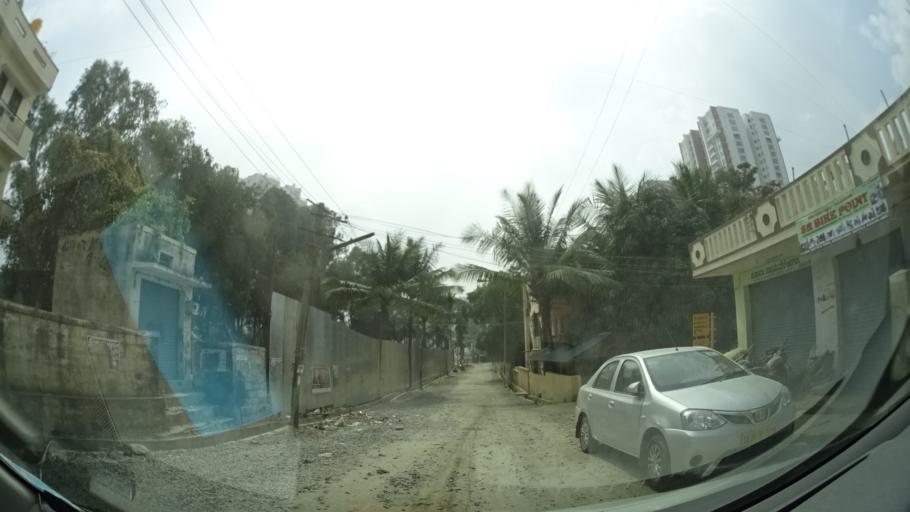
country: IN
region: Karnataka
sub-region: Bangalore Rural
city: Hoskote
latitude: 12.9779
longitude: 77.7532
